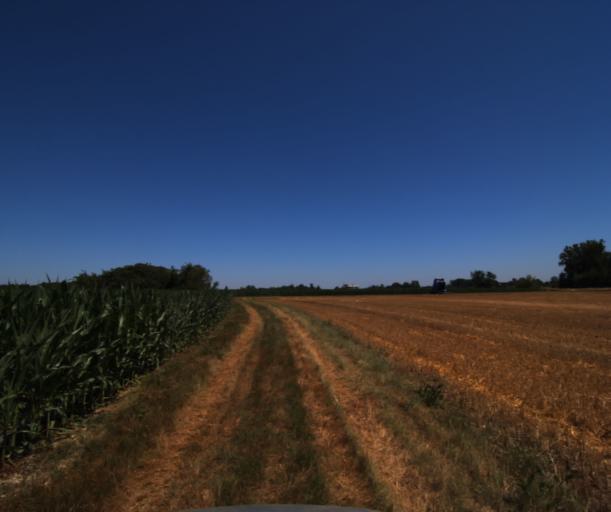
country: FR
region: Midi-Pyrenees
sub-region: Departement de la Haute-Garonne
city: Seysses
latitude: 43.4673
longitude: 1.2914
